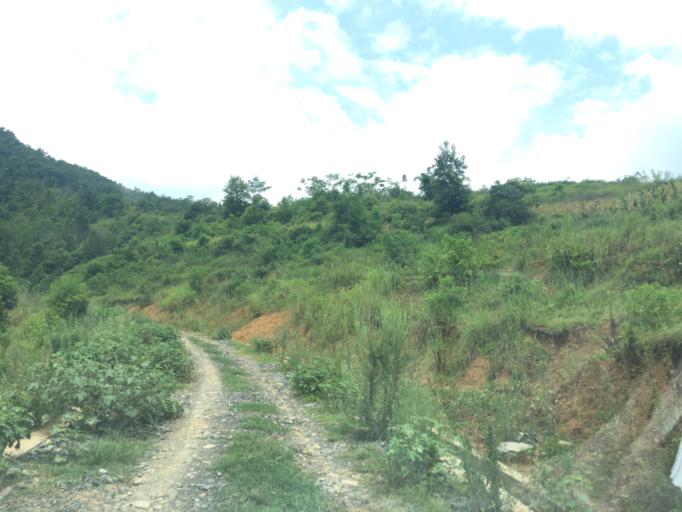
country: CN
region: Guangxi Zhuangzu Zizhiqu
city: Xinzhou
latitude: 25.1975
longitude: 105.7336
